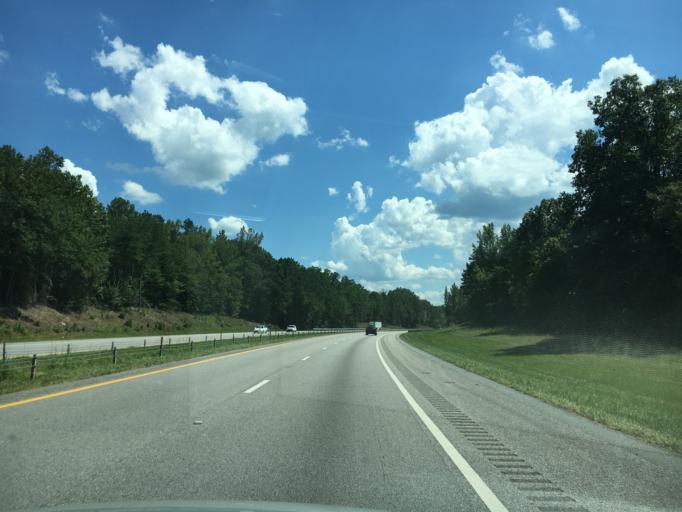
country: US
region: South Carolina
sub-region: Laurens County
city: Watts Mills
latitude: 34.6022
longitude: -81.8918
